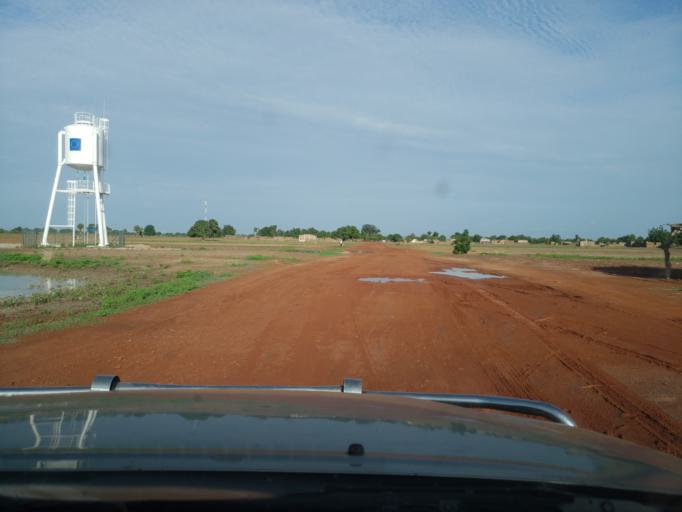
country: ML
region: Sikasso
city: Koutiala
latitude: 12.4231
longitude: -5.6761
